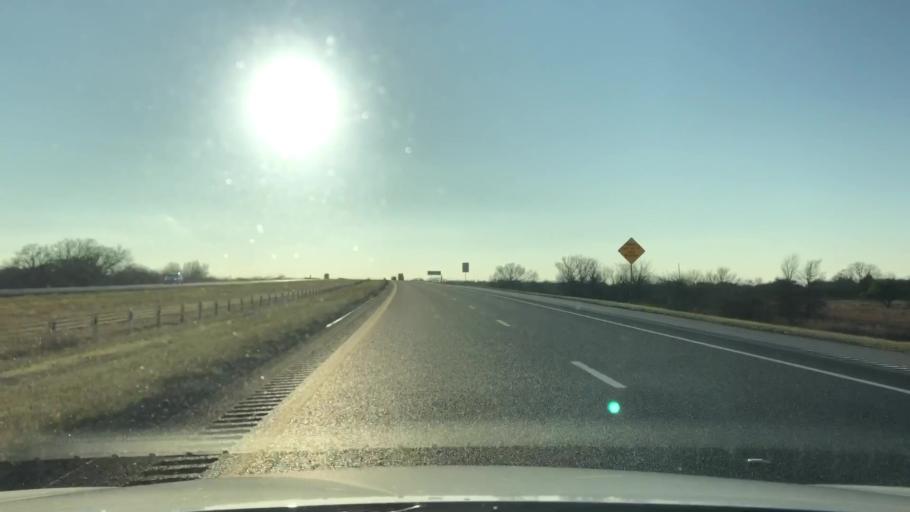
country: US
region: Texas
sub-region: Gonzales County
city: Waelder
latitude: 29.6847
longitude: -97.2647
